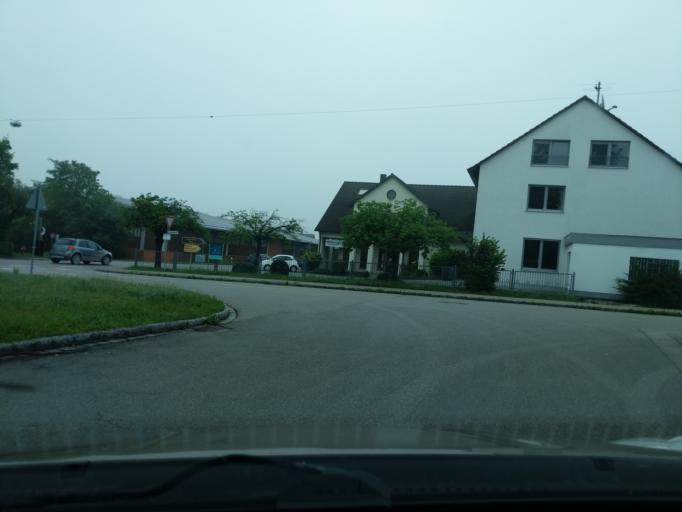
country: DE
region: Bavaria
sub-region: Swabia
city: Gessertshausen
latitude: 48.3314
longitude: 10.7374
